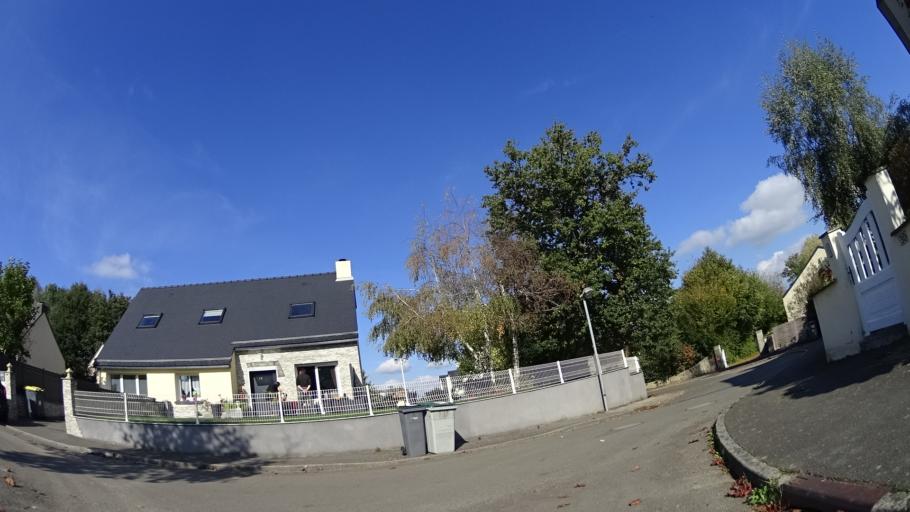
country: FR
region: Brittany
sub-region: Departement d'Ille-et-Vilaine
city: Geveze
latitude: 48.2226
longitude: -1.7909
